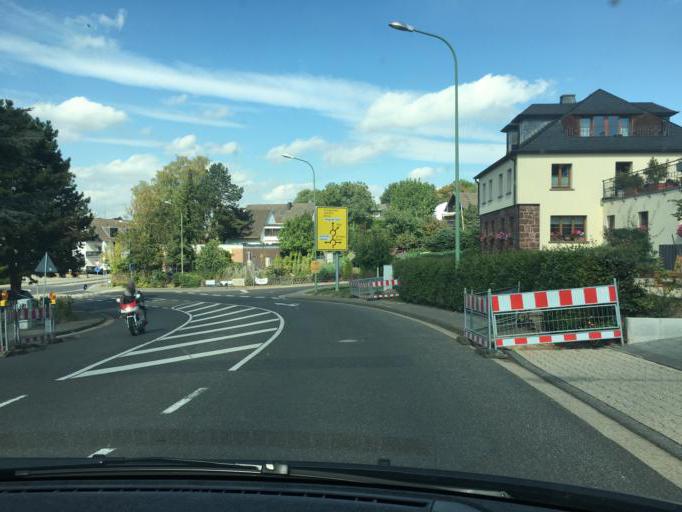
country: DE
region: North Rhine-Westphalia
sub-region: Regierungsbezirk Koln
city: Nideggen
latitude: 50.6916
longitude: 6.4851
